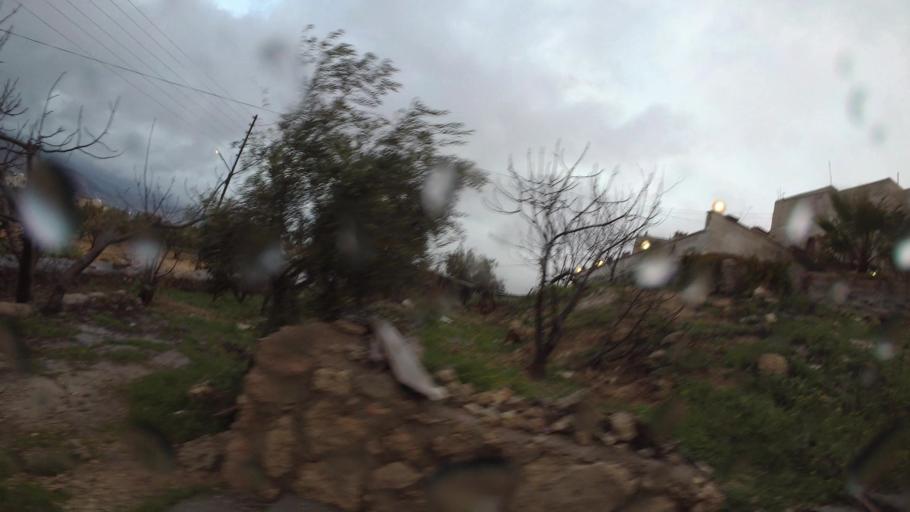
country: JO
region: Amman
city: Al Jubayhah
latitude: 32.0338
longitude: 35.8451
